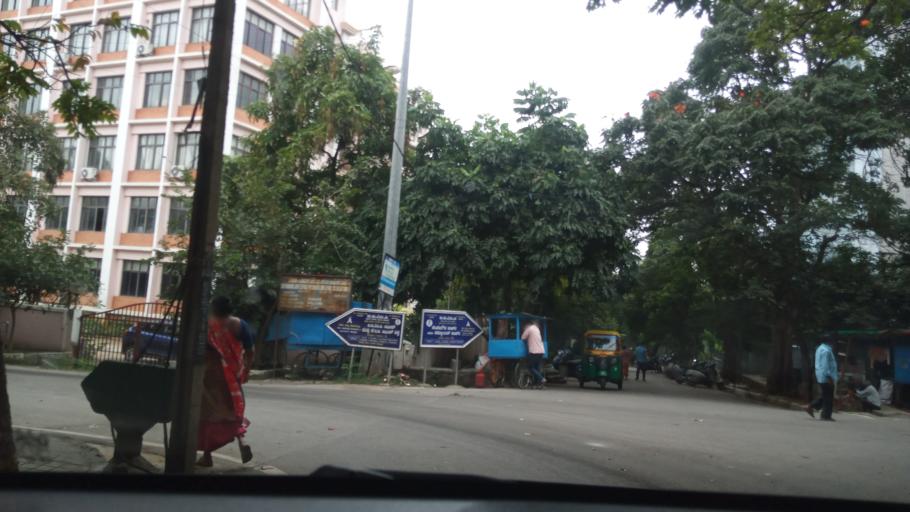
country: IN
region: Karnataka
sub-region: Bangalore Urban
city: Bangalore
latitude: 13.0125
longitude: 77.5376
